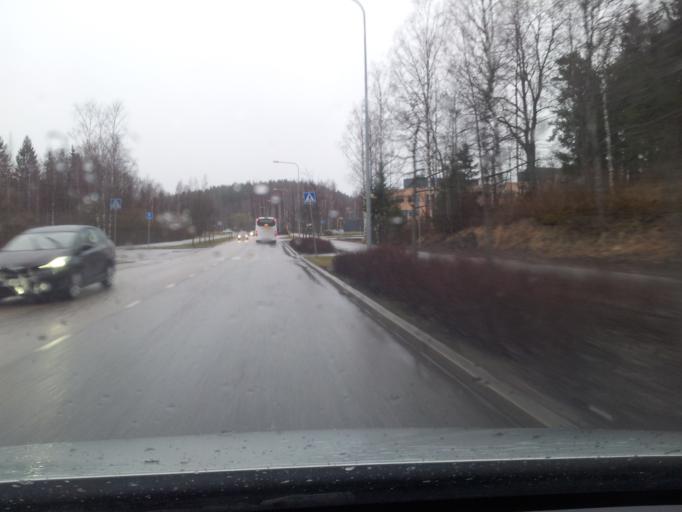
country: FI
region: Uusimaa
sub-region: Helsinki
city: Espoo
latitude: 60.1822
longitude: 24.6127
